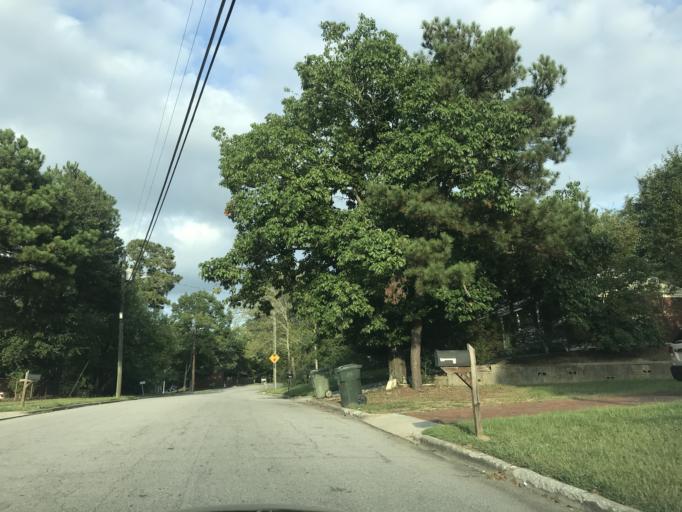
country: US
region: North Carolina
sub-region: Wake County
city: Raleigh
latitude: 35.7513
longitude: -78.6187
